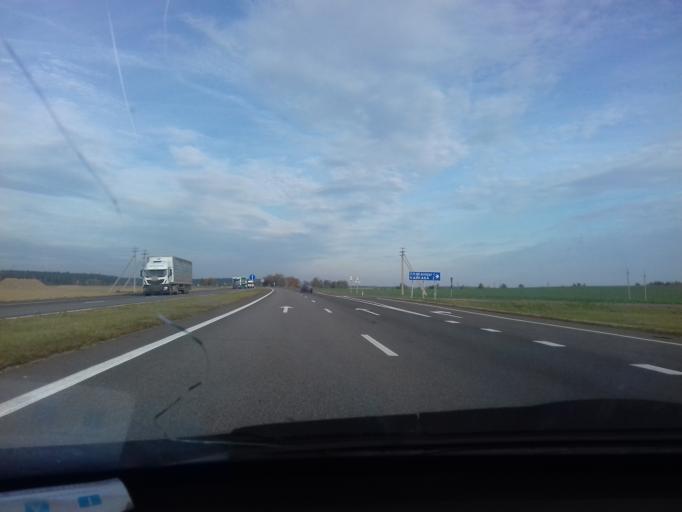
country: BY
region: Minsk
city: Machulishchy
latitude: 53.7400
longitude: 27.6119
